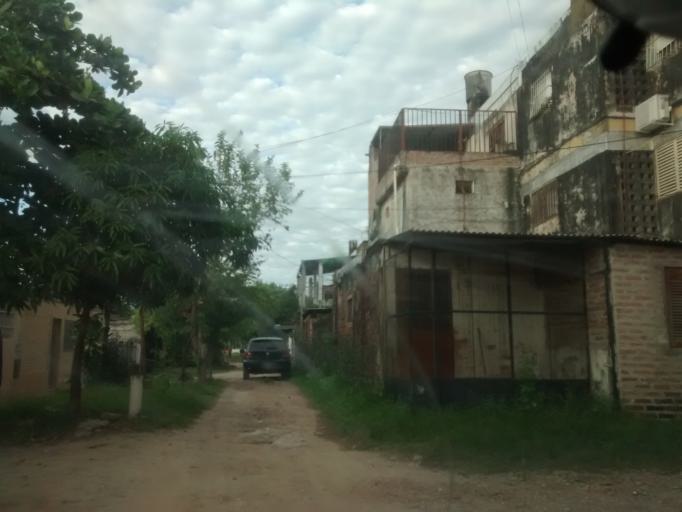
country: AR
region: Chaco
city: Fontana
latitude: -27.4470
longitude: -59.0138
